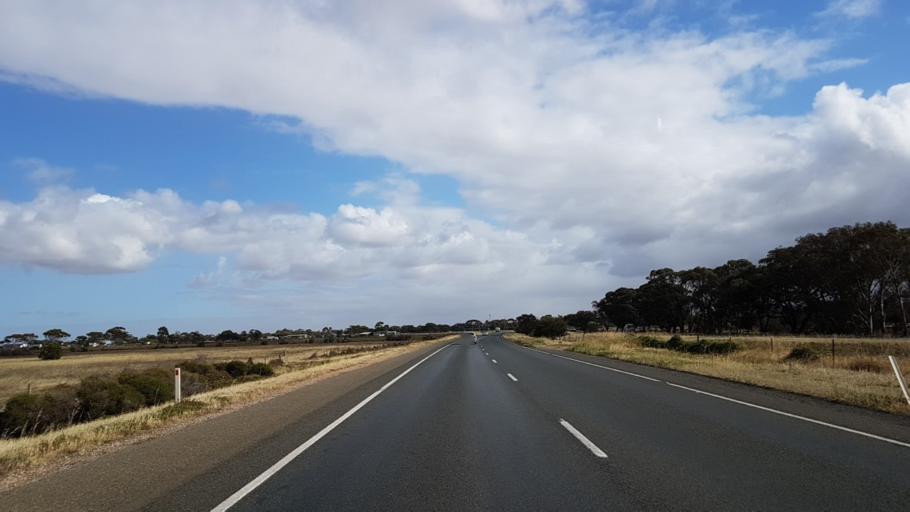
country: AU
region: South Australia
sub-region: Mallala
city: Two Wells
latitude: -34.6094
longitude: 138.5164
